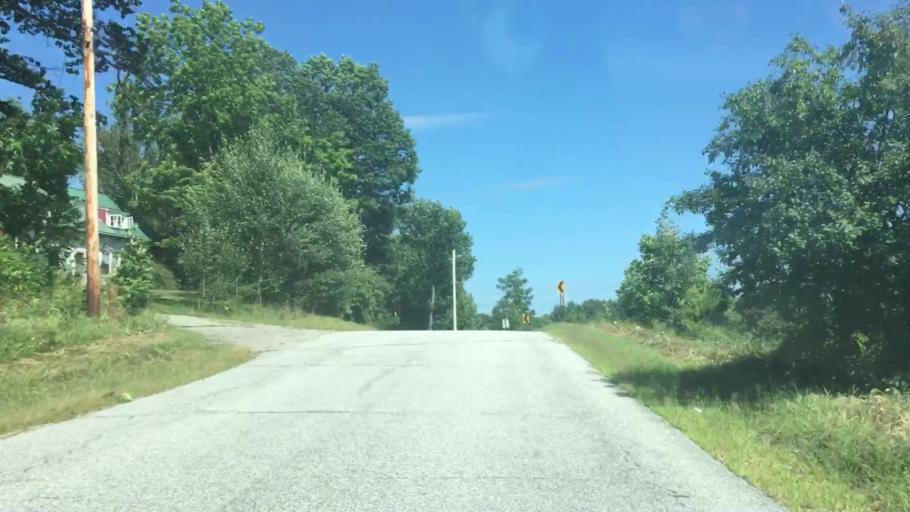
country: US
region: Maine
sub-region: Kennebec County
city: Monmouth
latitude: 44.2048
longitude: -69.9547
